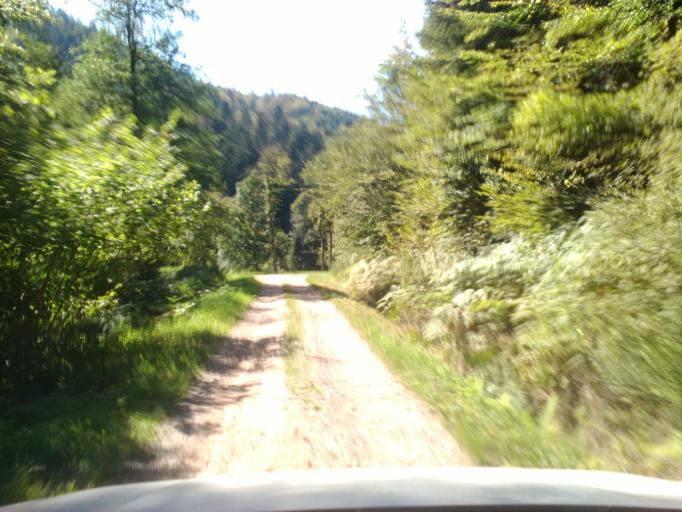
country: FR
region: Lorraine
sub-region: Departement des Vosges
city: Senones
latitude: 48.4240
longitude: 6.9508
